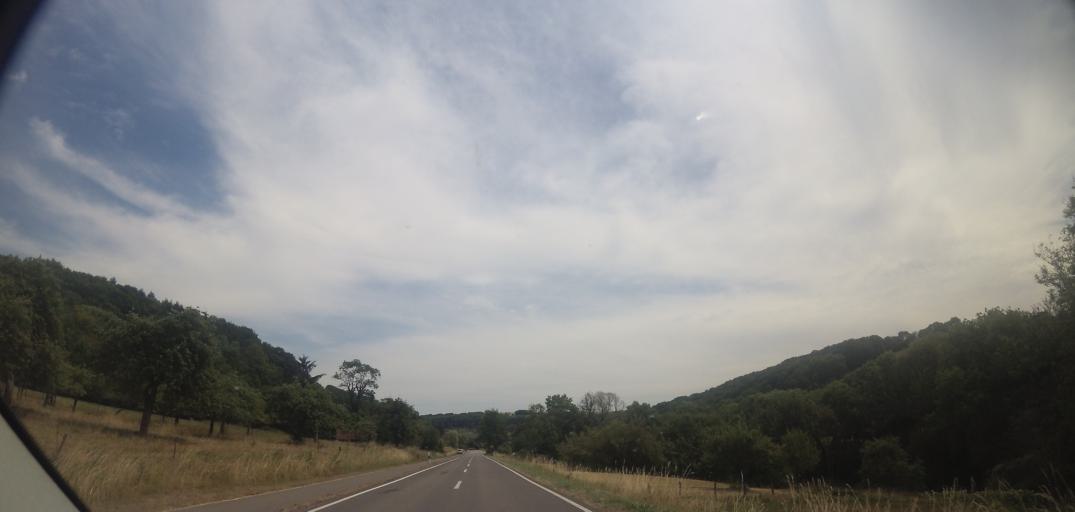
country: DE
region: Saarland
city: Merzig
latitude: 49.4199
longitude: 6.5832
